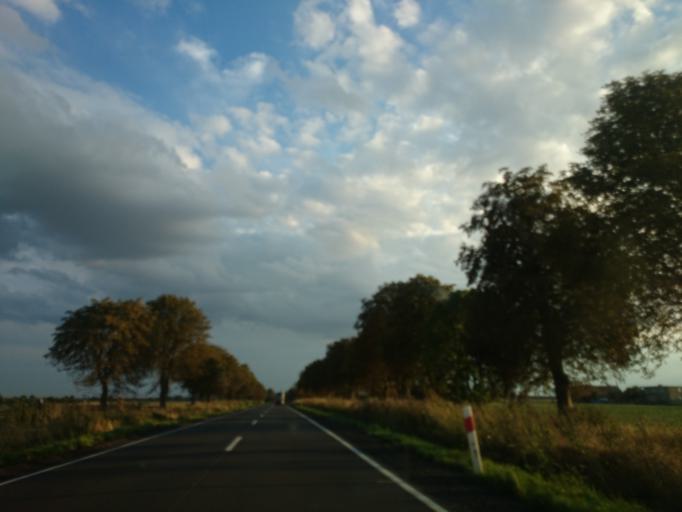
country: PL
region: West Pomeranian Voivodeship
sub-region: Powiat mysliborski
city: Debno
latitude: 52.6732
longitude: 14.6815
